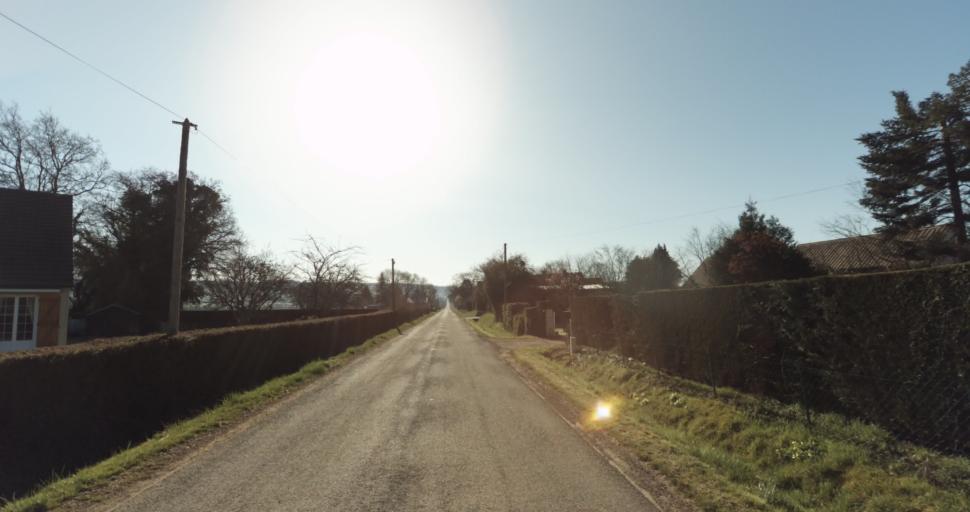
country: FR
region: Lower Normandy
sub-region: Departement du Calvados
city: Saint-Pierre-sur-Dives
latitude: 48.9995
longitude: 0.0039
